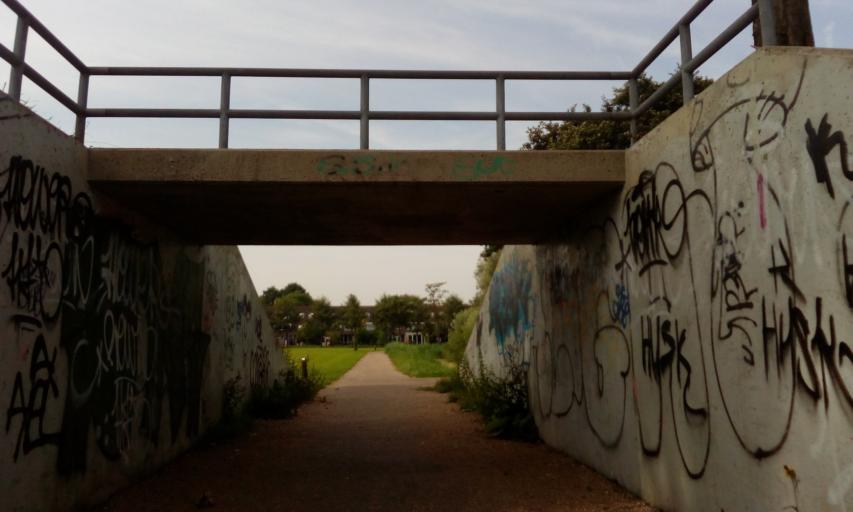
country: NL
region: South Holland
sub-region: Gemeente Capelle aan den IJssel
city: Capelle aan den IJssel
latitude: 51.9708
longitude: 4.5688
